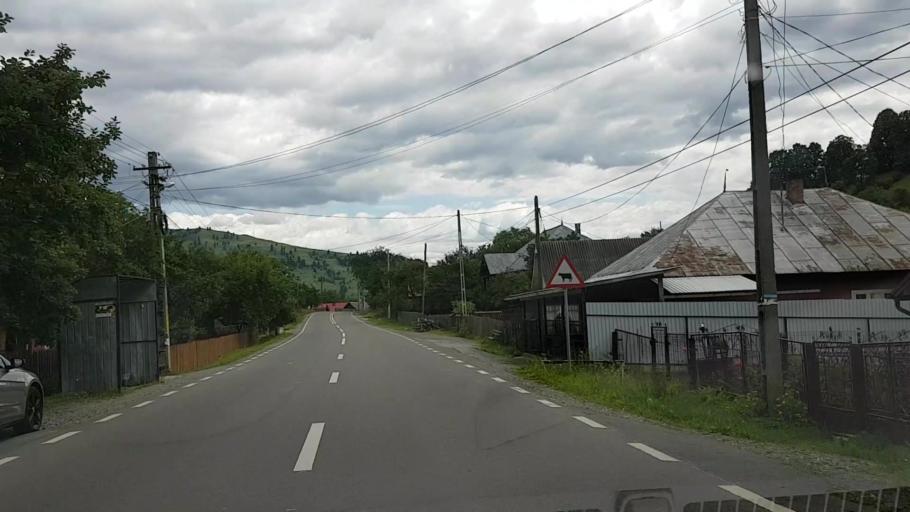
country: RO
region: Neamt
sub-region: Comuna Borca
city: Borca
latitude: 47.1916
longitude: 25.7693
